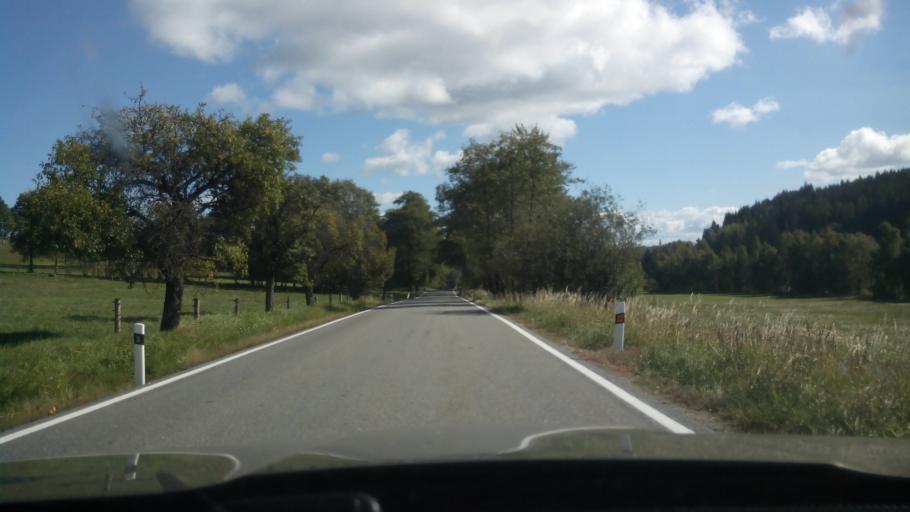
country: CZ
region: Jihocesky
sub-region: Okres Prachatice
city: Stachy
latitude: 49.1187
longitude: 13.6377
